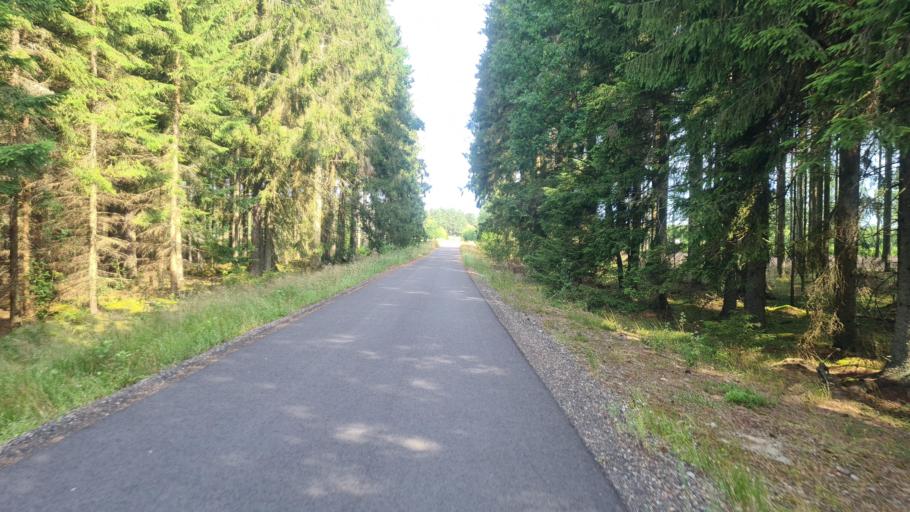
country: SE
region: Kronoberg
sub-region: Ljungby Kommun
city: Ljungby
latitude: 56.8625
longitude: 13.9778
